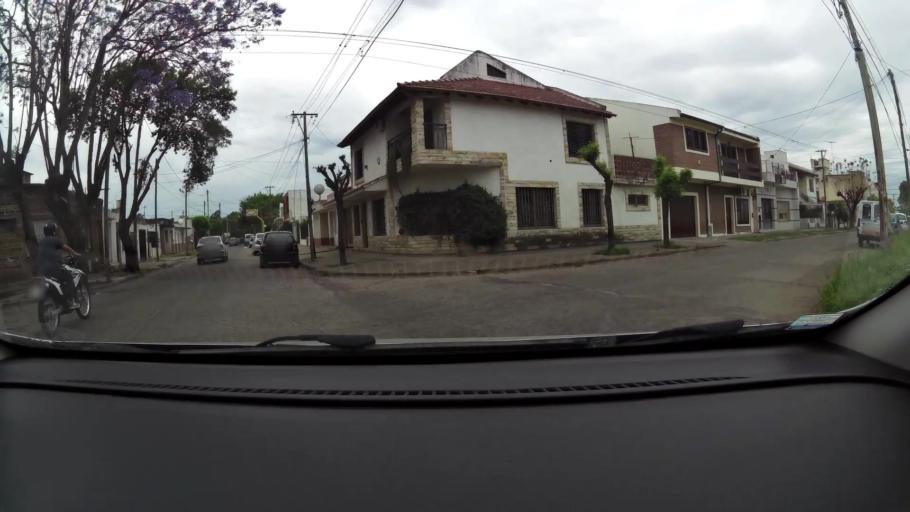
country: AR
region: Buenos Aires
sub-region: Partido de Zarate
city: Zarate
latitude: -34.0917
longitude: -59.0320
